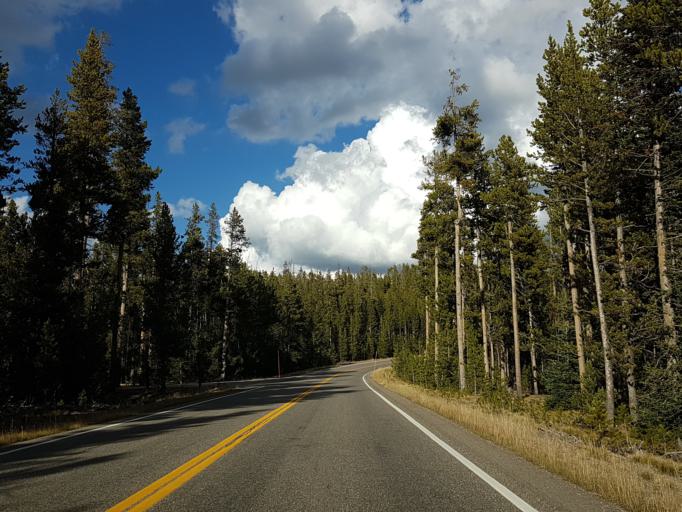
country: US
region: Montana
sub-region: Gallatin County
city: West Yellowstone
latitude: 44.4478
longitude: -110.6976
